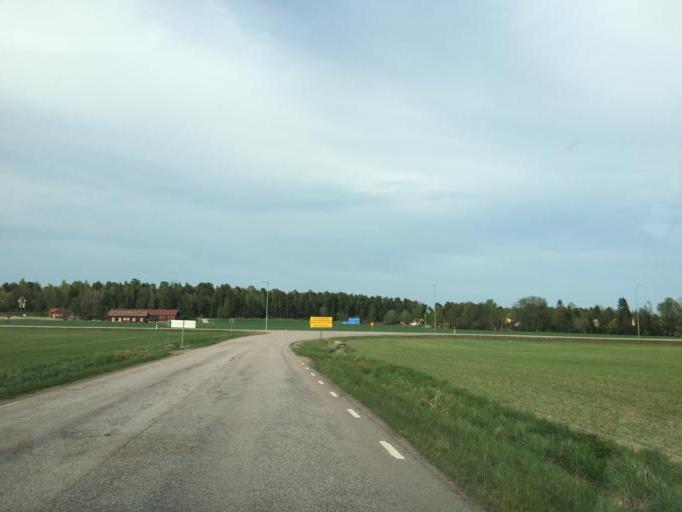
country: SE
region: Vaestmanland
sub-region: Hallstahammars Kommun
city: Hallstahammar
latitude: 59.6059
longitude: 16.2003
